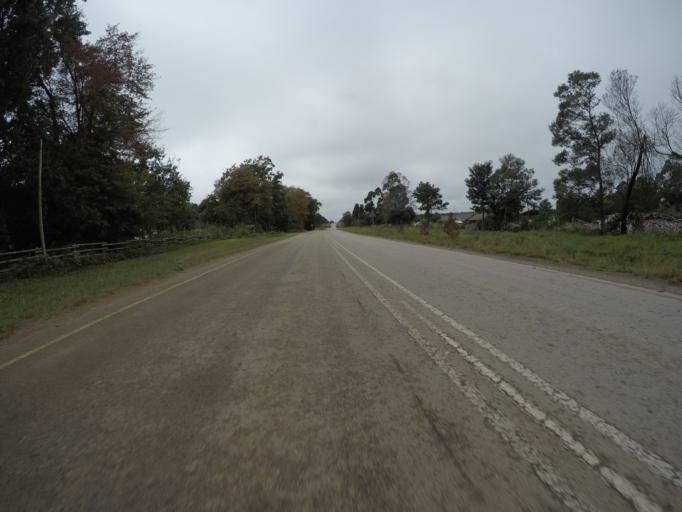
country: ZA
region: Eastern Cape
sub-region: Cacadu District Municipality
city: Kareedouw
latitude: -33.9945
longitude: 24.1192
